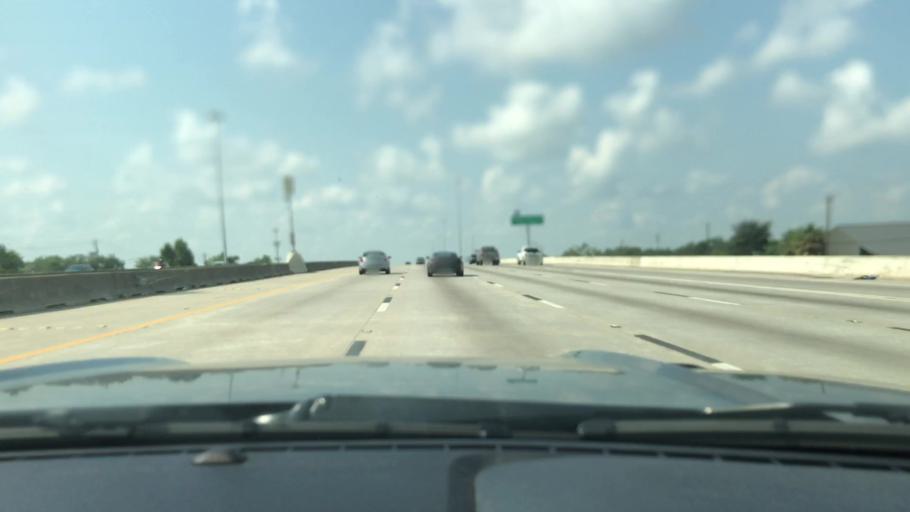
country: US
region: Texas
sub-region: Harris County
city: Aldine
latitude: 29.8819
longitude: -95.3234
